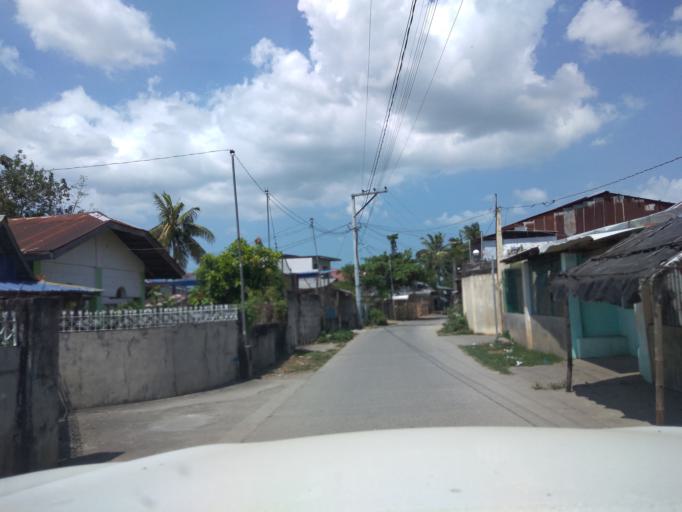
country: PH
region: Central Luzon
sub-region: Province of Pampanga
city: Bahay Pare
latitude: 15.0160
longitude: 120.8714
